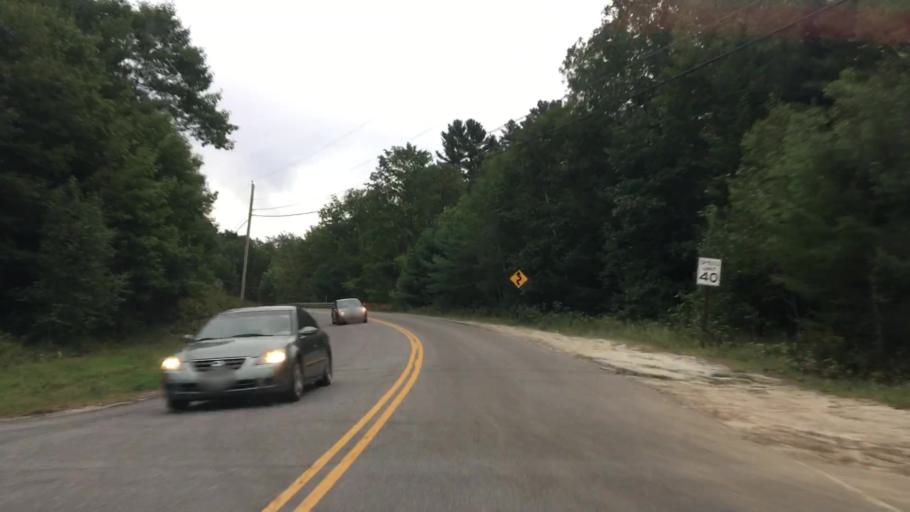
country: US
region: Maine
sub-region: Cumberland County
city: New Gloucester
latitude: 43.9017
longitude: -70.2058
